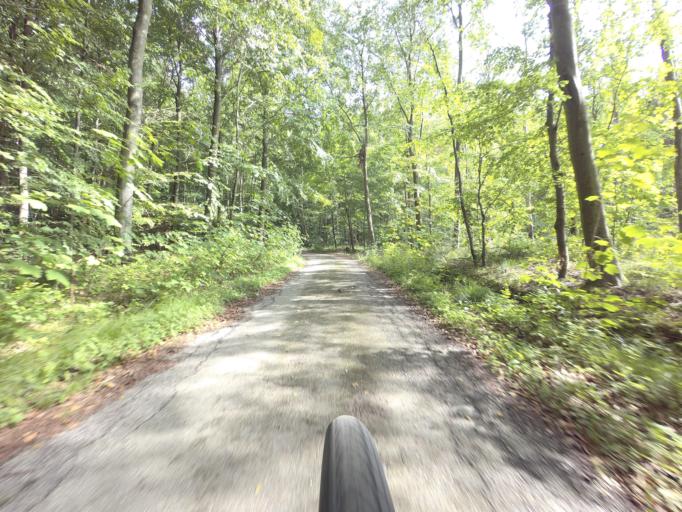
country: DK
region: Zealand
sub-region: Faxe Kommune
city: Fakse Ladeplads
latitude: 55.2355
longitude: 12.1866
